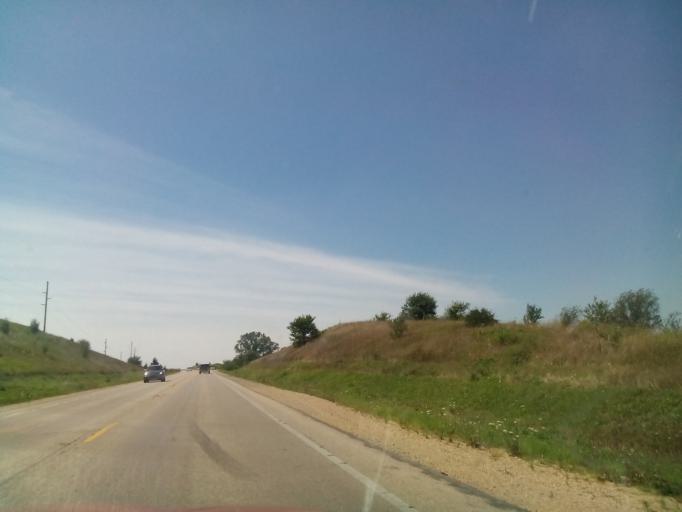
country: US
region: Wisconsin
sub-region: Green County
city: Monroe
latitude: 42.6571
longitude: -89.6279
